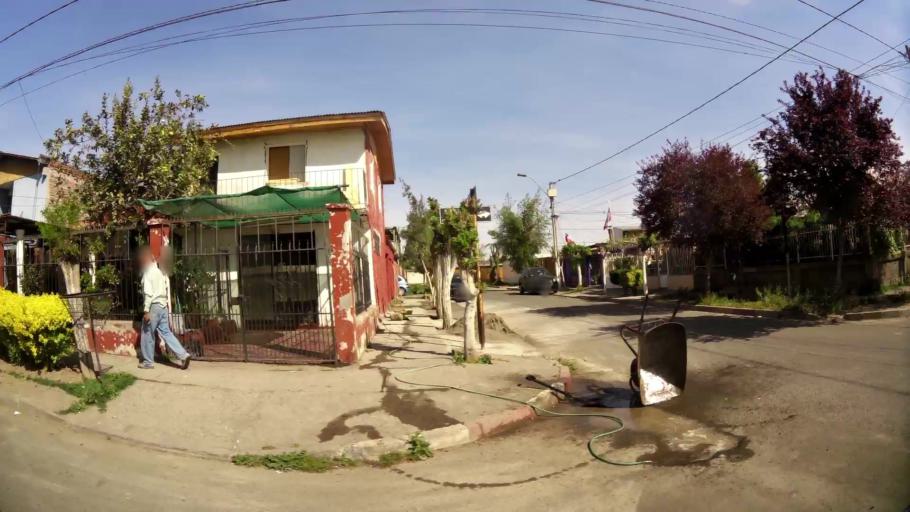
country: CL
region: Santiago Metropolitan
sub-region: Provincia de Santiago
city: La Pintana
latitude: -33.5391
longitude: -70.6281
